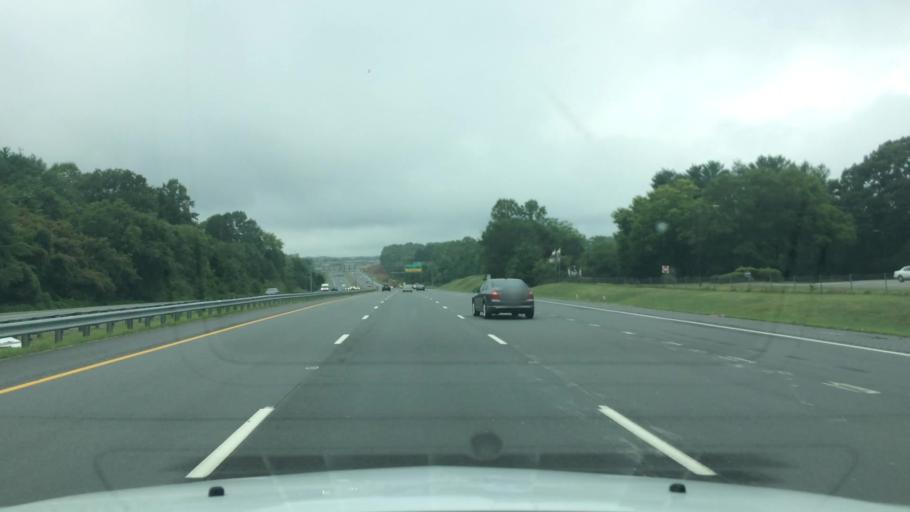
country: US
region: North Carolina
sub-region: Forsyth County
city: Clemmons
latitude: 36.0728
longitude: -80.3423
